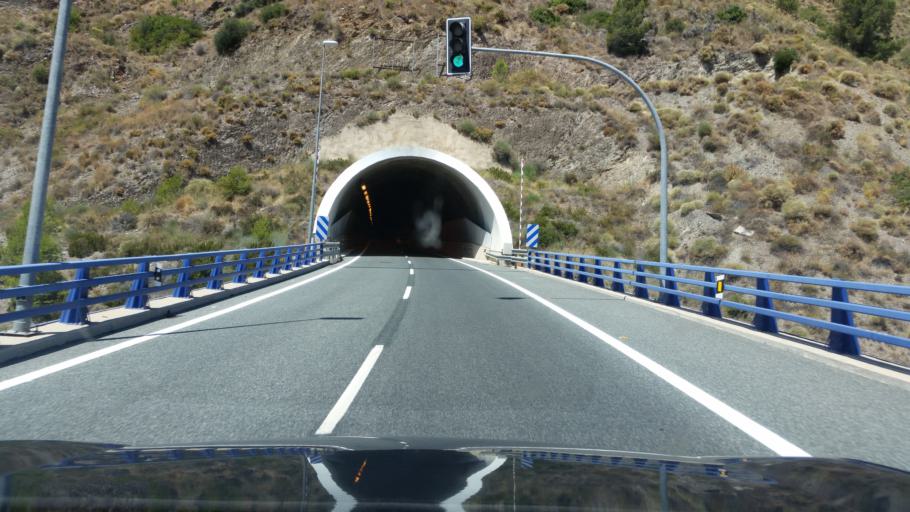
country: ES
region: Andalusia
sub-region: Provincia de Granada
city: Polopos
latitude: 36.7514
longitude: -3.3229
